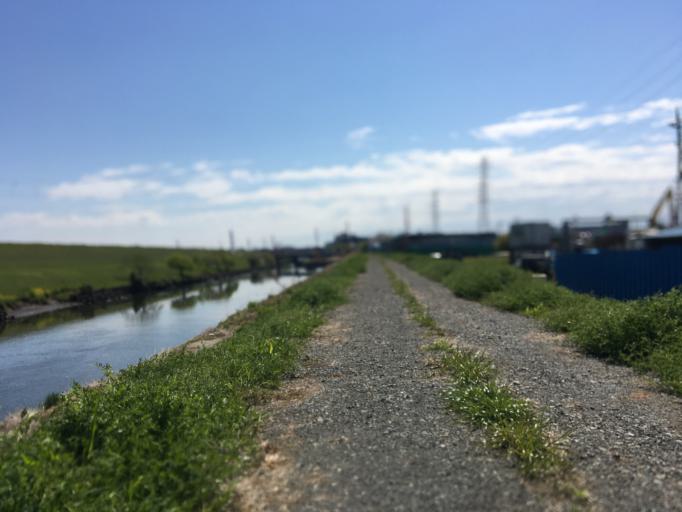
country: JP
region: Saitama
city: Wako
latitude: 35.8004
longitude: 139.6351
